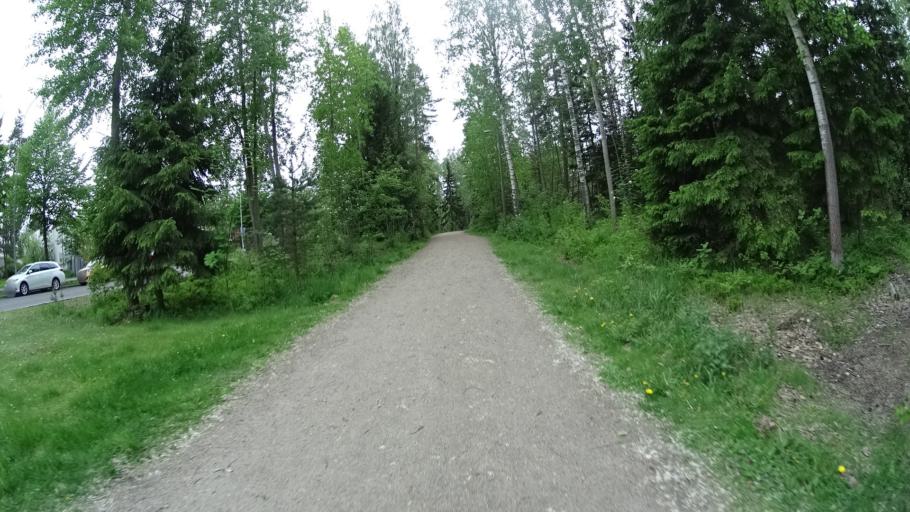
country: FI
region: Uusimaa
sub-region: Helsinki
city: Vantaa
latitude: 60.2474
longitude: 25.0751
